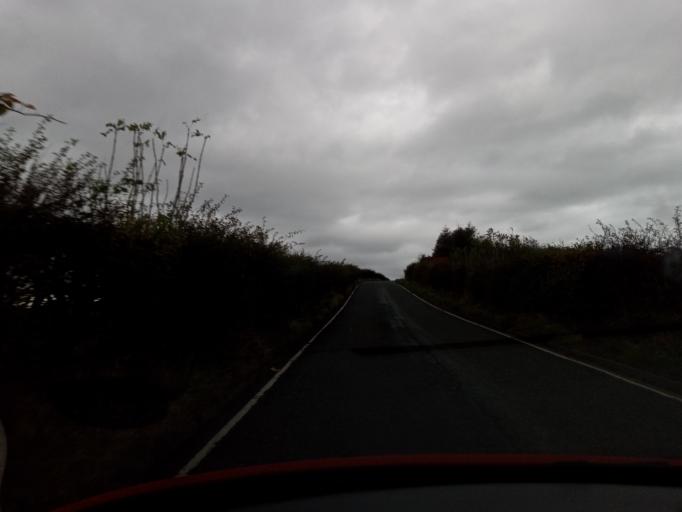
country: GB
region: Scotland
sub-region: West Lothian
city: Bathgate
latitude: 55.9192
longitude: -3.6368
